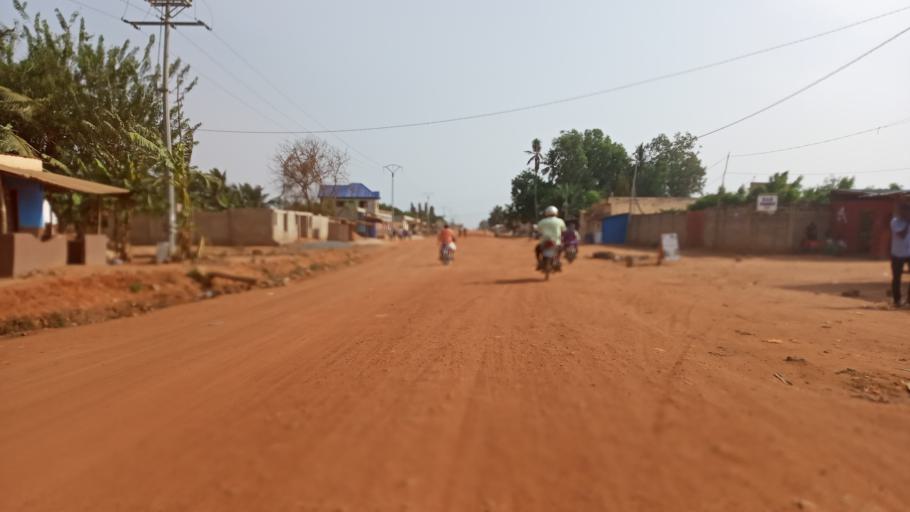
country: TG
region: Maritime
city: Lome
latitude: 6.1930
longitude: 1.1258
